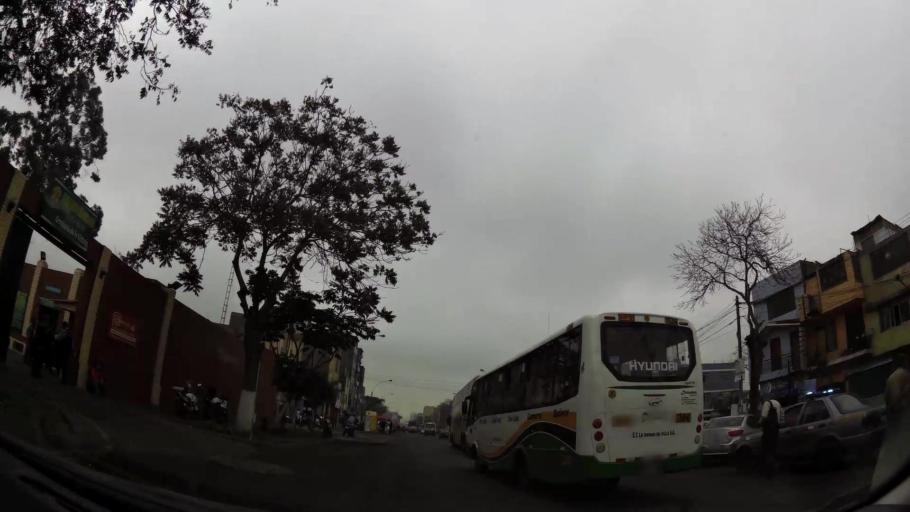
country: PE
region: Lima
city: Lima
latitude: -12.0628
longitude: -77.0259
